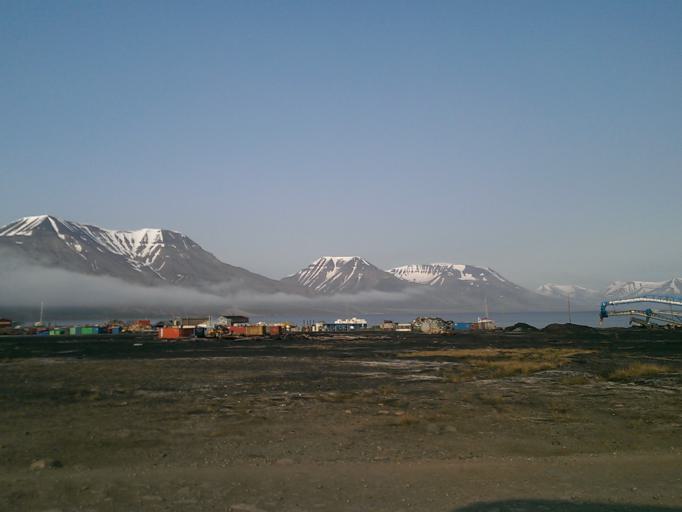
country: SJ
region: Svalbard
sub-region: Spitsbergen
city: Longyearbyen
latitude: 78.2449
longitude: 15.5324
